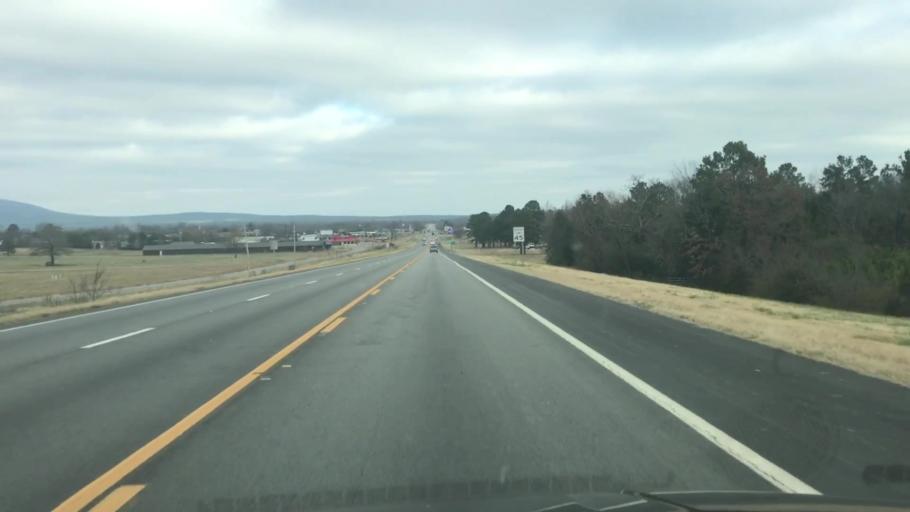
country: US
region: Arkansas
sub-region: Scott County
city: Waldron
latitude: 34.8916
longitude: -94.1076
